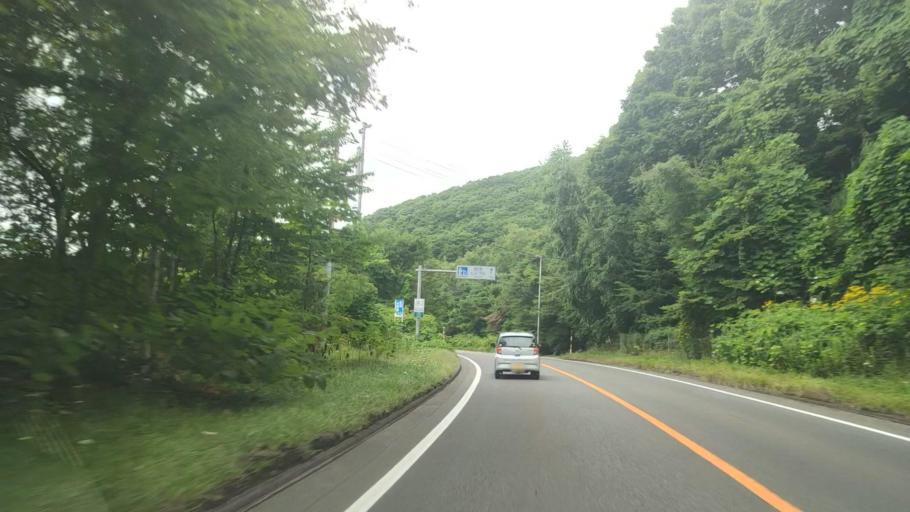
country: JP
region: Hokkaido
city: Date
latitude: 42.5667
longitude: 140.7364
